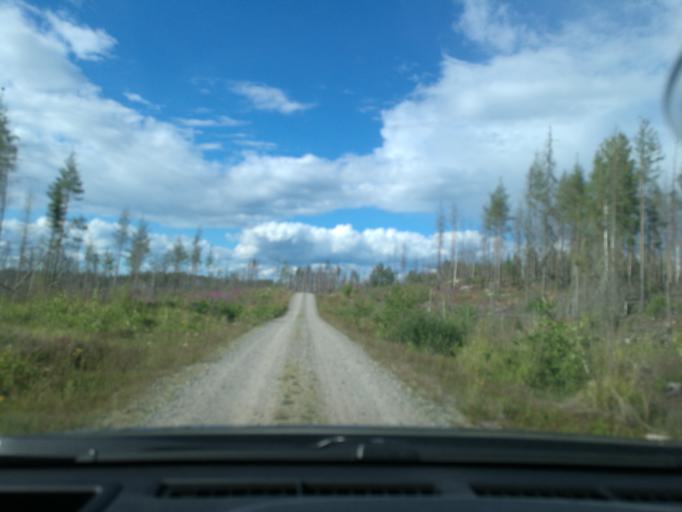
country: SE
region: Vaestmanland
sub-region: Surahammars Kommun
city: Ramnas
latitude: 59.8517
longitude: 16.2501
